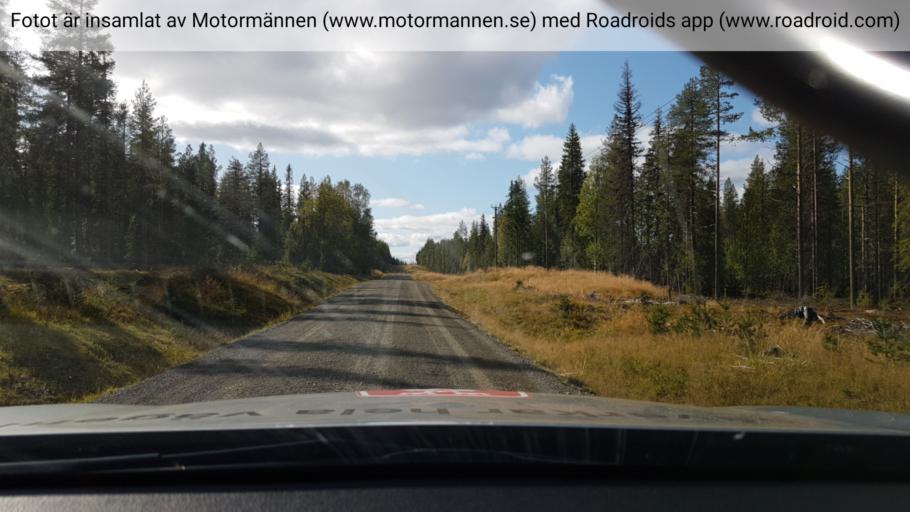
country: SE
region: Vaesterbotten
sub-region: Mala Kommun
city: Mala
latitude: 65.4906
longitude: 18.2527
